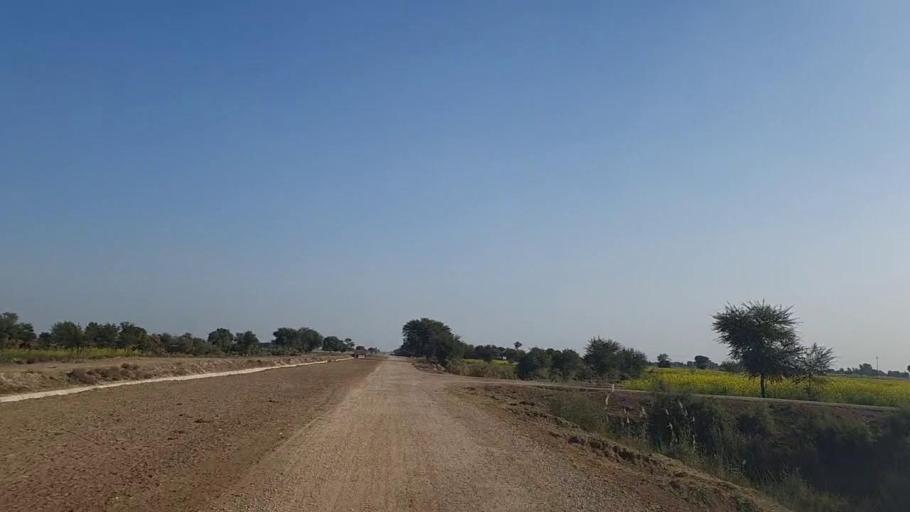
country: PK
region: Sindh
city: Shahpur Chakar
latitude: 26.1998
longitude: 68.6500
